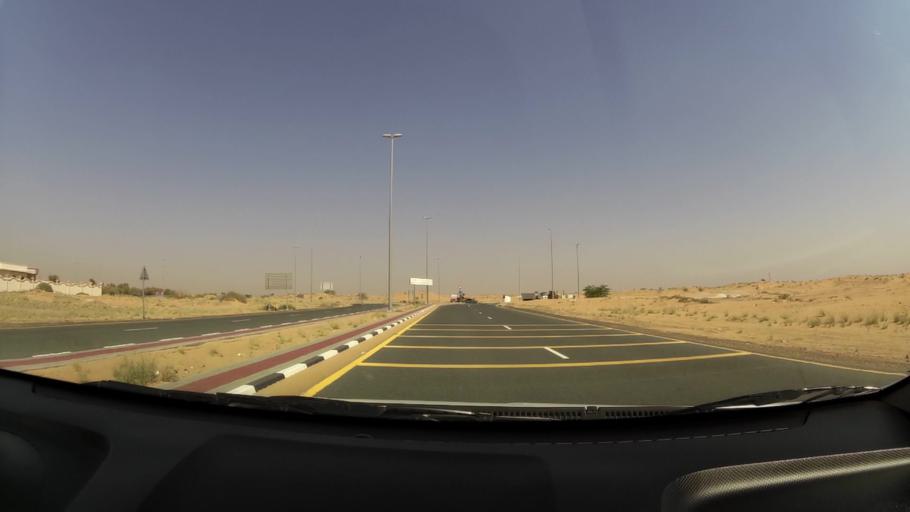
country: AE
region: Umm al Qaywayn
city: Umm al Qaywayn
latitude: 25.4696
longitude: 55.6134
